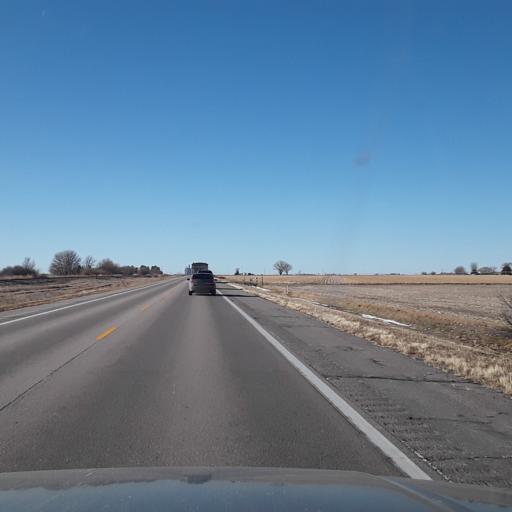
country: US
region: Nebraska
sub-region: Kearney County
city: Minden
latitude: 40.4991
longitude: -98.9779
